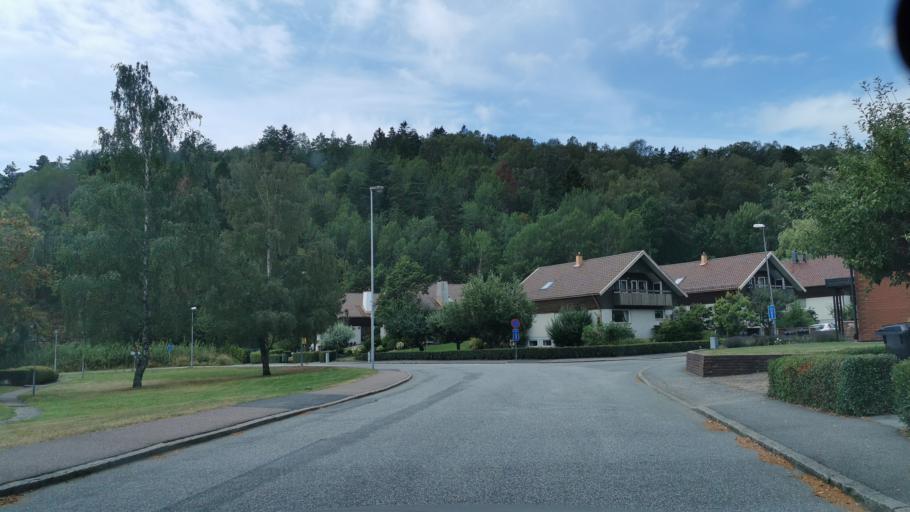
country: SE
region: Vaestra Goetaland
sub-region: Molndal
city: Moelndal
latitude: 57.6654
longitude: 11.9883
